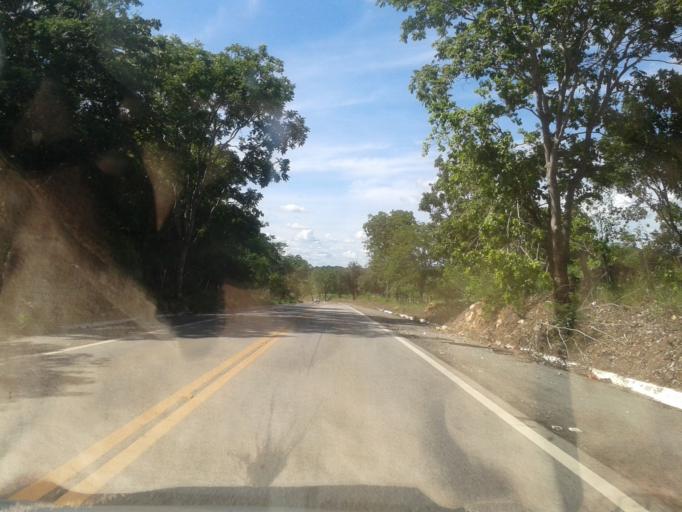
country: BR
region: Goias
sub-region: Itapuranga
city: Itapuranga
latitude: -15.3933
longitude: -50.3862
